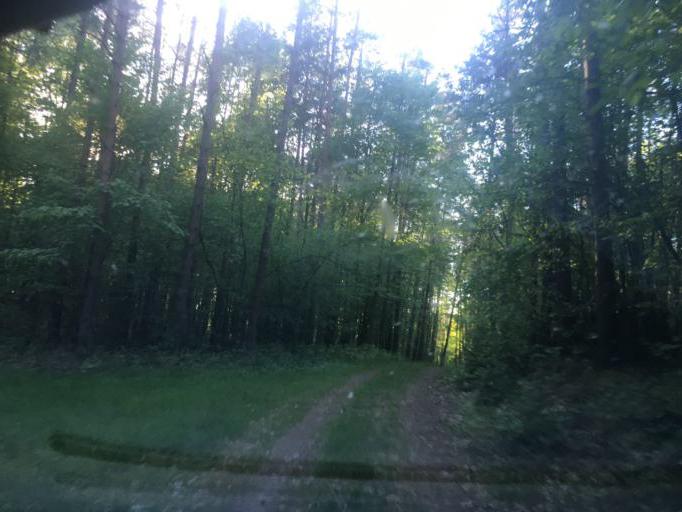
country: PL
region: Kujawsko-Pomorskie
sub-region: Powiat brodnicki
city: Gorzno
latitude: 53.2163
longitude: 19.7257
